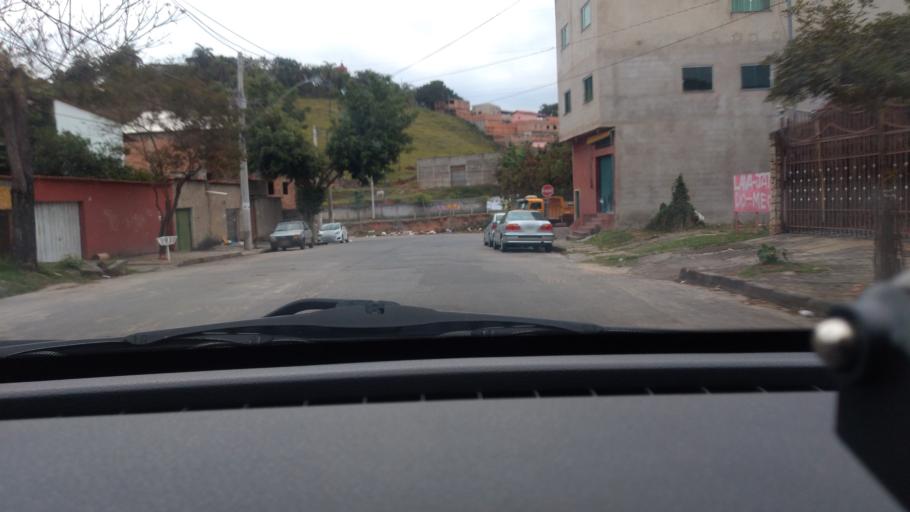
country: BR
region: Minas Gerais
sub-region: Belo Horizonte
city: Belo Horizonte
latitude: -19.8224
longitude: -43.9366
